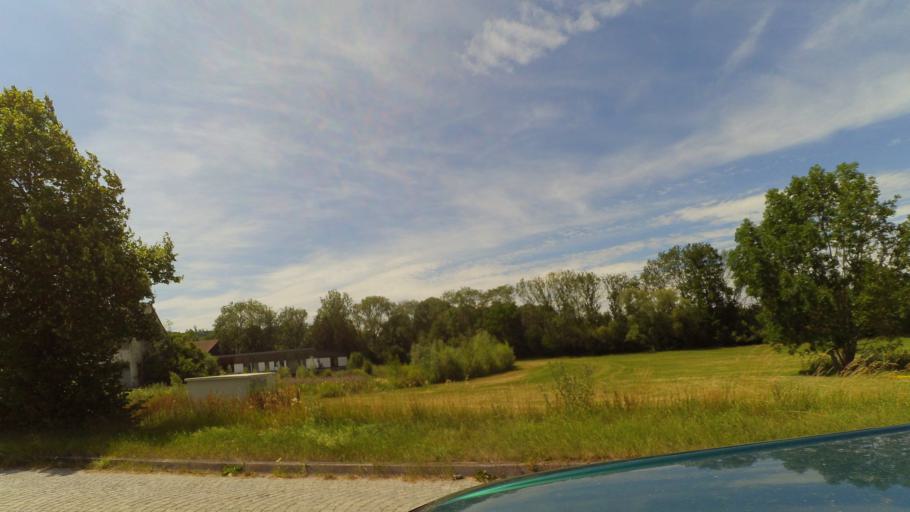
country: DE
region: Baden-Wuerttemberg
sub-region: Regierungsbezirk Stuttgart
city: Gaildorf
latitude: 48.9944
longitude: 9.7807
